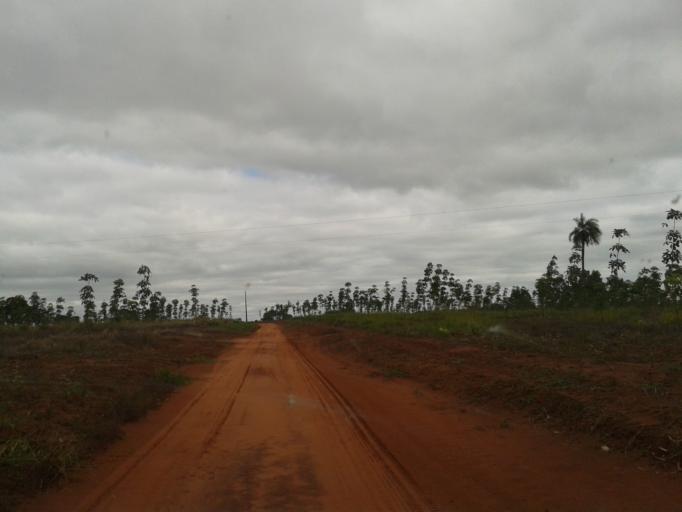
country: BR
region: Minas Gerais
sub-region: Campina Verde
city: Campina Verde
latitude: -19.5201
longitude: -49.6293
